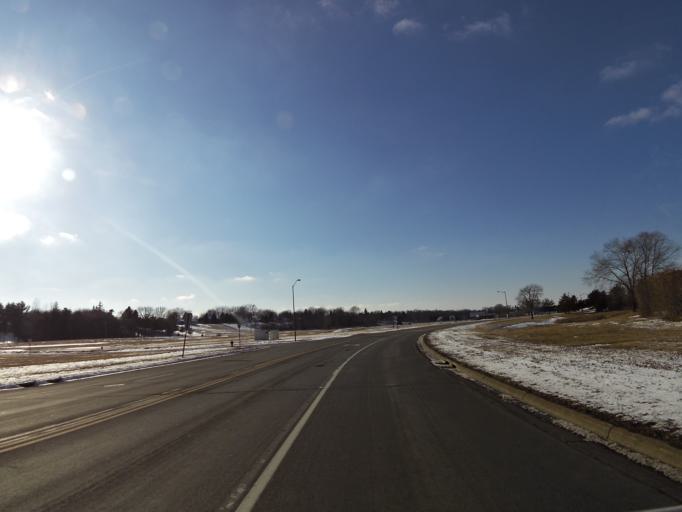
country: US
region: Minnesota
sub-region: Scott County
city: Shakopee
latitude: 44.7850
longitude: -93.4800
